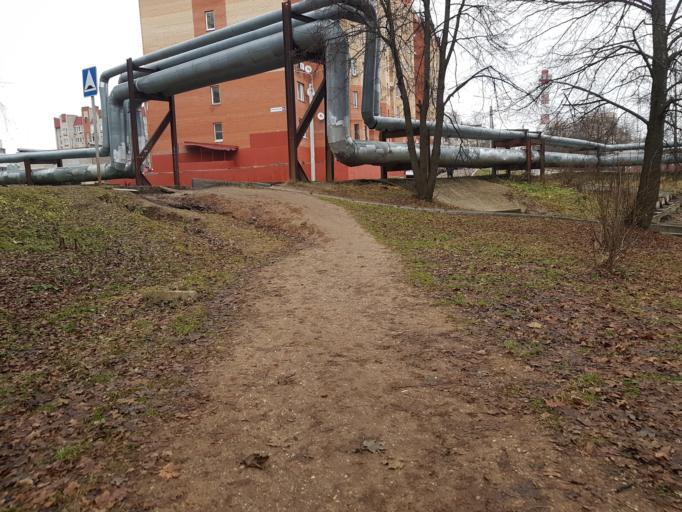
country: RU
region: Moskovskaya
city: Istra
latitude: 55.9077
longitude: 36.8697
